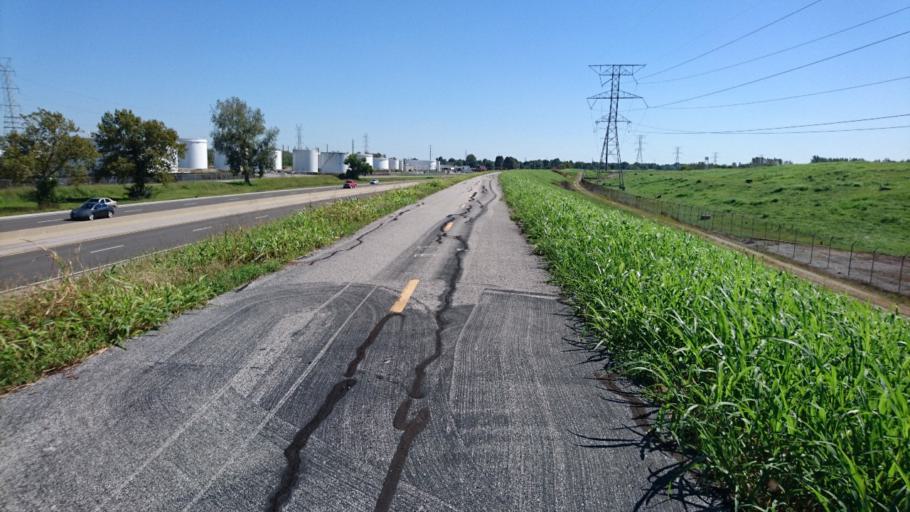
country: US
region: Illinois
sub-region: Madison County
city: Wood River
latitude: 38.8475
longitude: -90.0998
